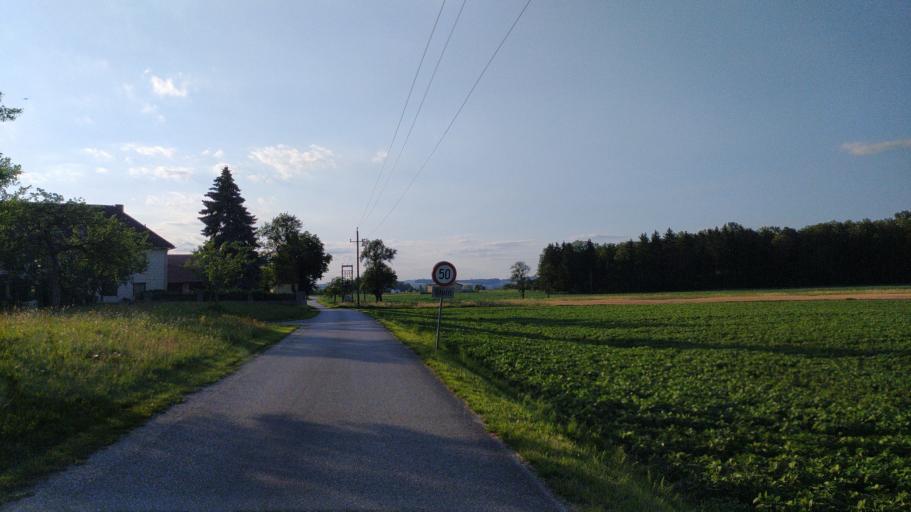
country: AT
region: Lower Austria
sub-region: Politischer Bezirk Amstetten
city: Ennsdorf
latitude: 48.2231
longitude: 14.5650
